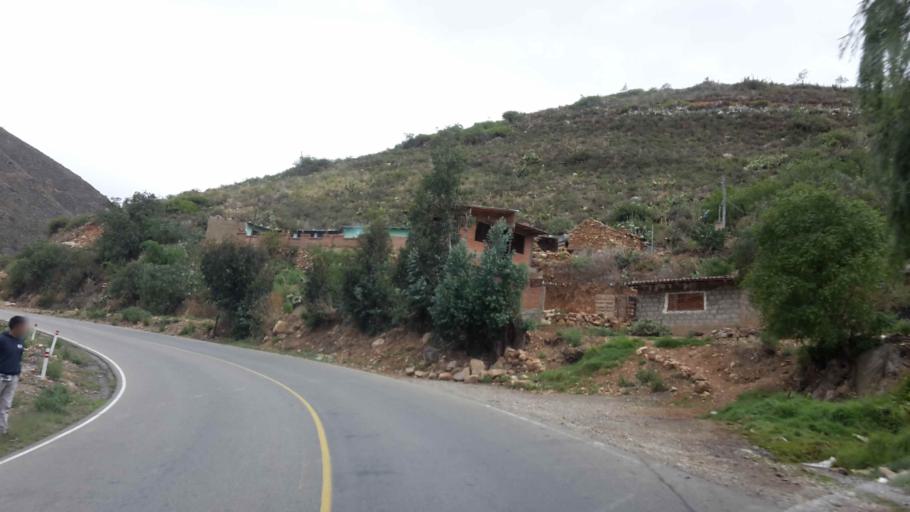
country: BO
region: Cochabamba
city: Punata
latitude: -17.5055
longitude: -65.7982
